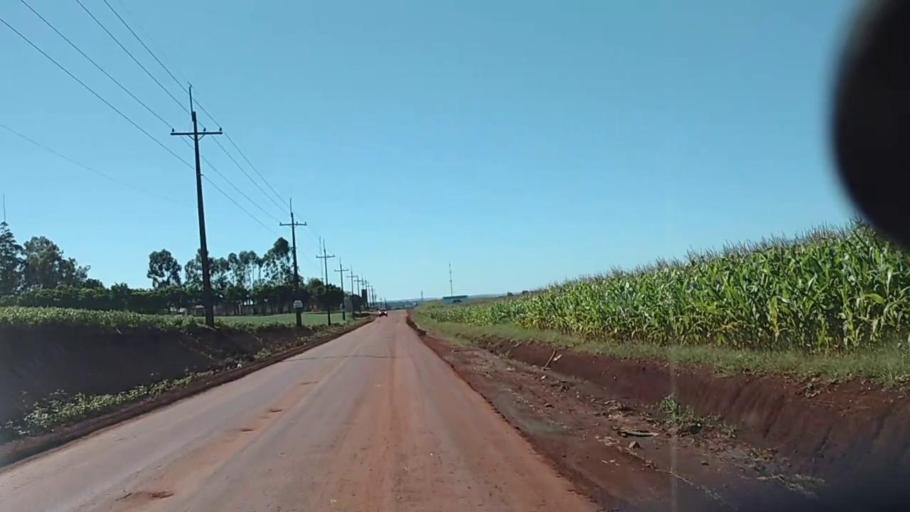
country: PY
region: Alto Parana
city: Naranjal
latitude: -25.9749
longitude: -55.2155
